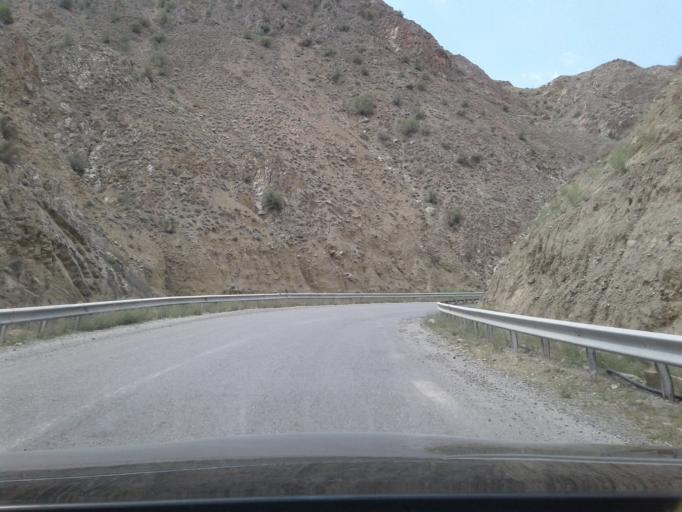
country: TM
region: Ahal
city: Baharly
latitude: 38.5022
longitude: 57.0508
